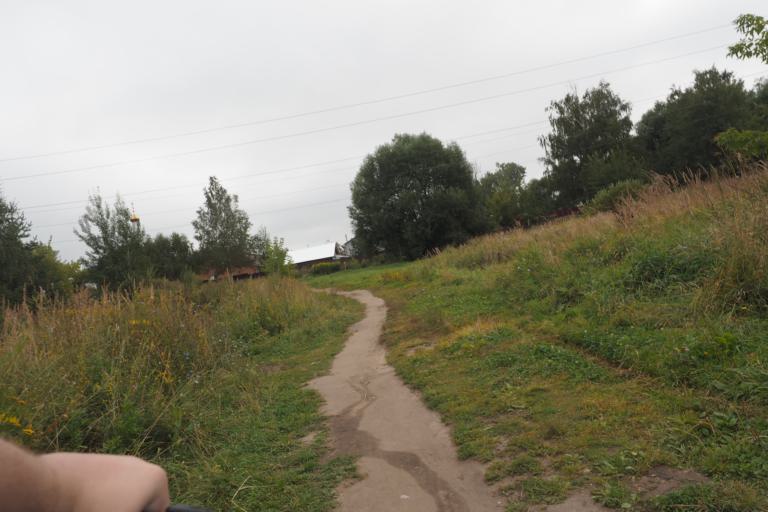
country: RU
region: Moskovskaya
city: Malyshevo
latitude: 55.5392
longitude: 38.3230
